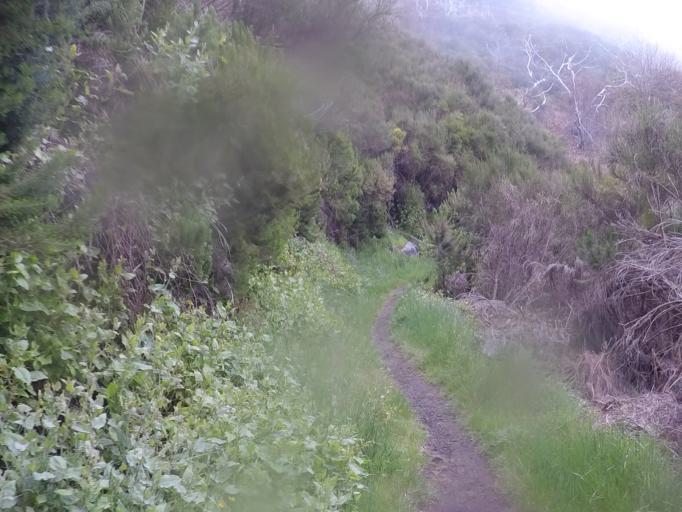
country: PT
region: Madeira
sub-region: Camara de Lobos
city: Curral das Freiras
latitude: 32.7264
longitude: -16.9849
